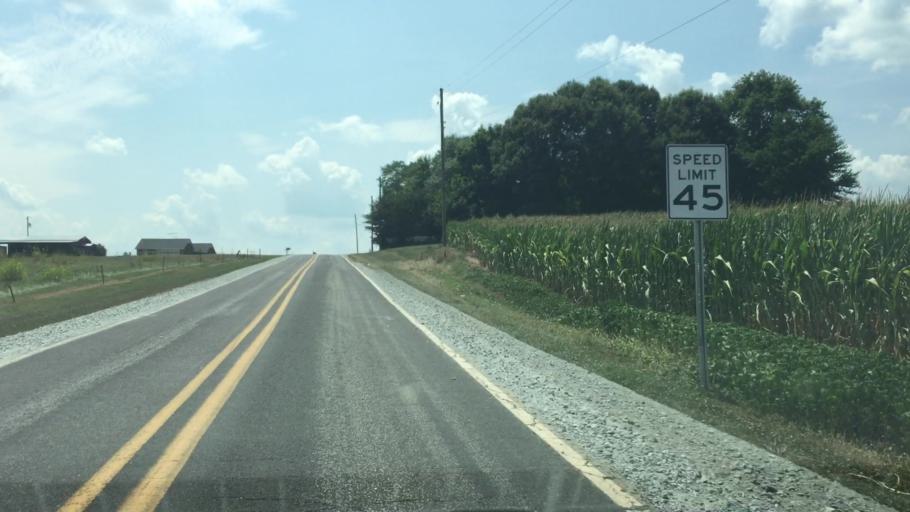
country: US
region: North Carolina
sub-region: Rowan County
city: China Grove
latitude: 35.6487
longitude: -80.6498
